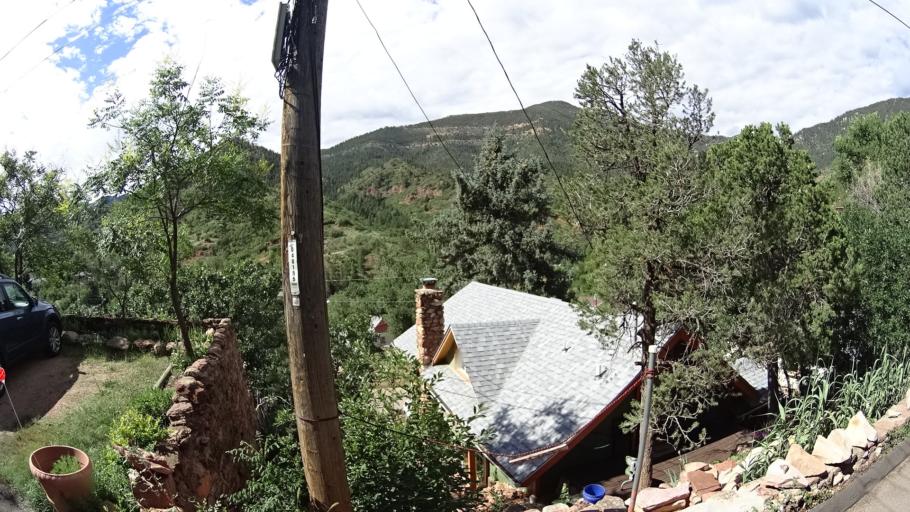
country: US
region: Colorado
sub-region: El Paso County
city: Manitou Springs
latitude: 38.8603
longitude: -104.9232
